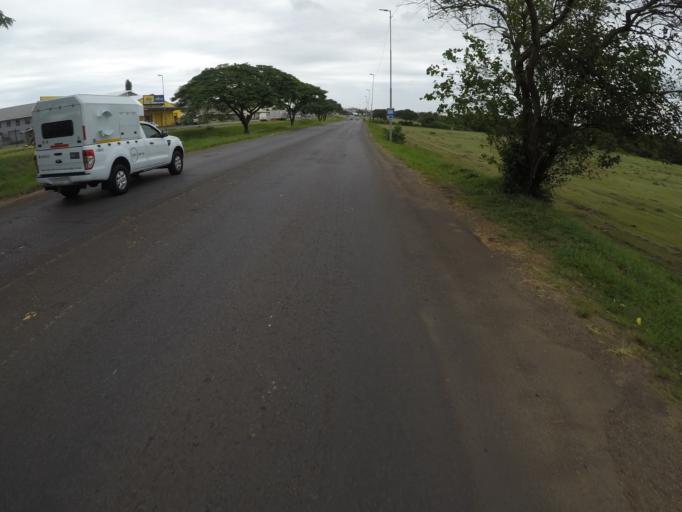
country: ZA
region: KwaZulu-Natal
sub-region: uThungulu District Municipality
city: Empangeni
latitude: -28.7693
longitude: 31.9037
